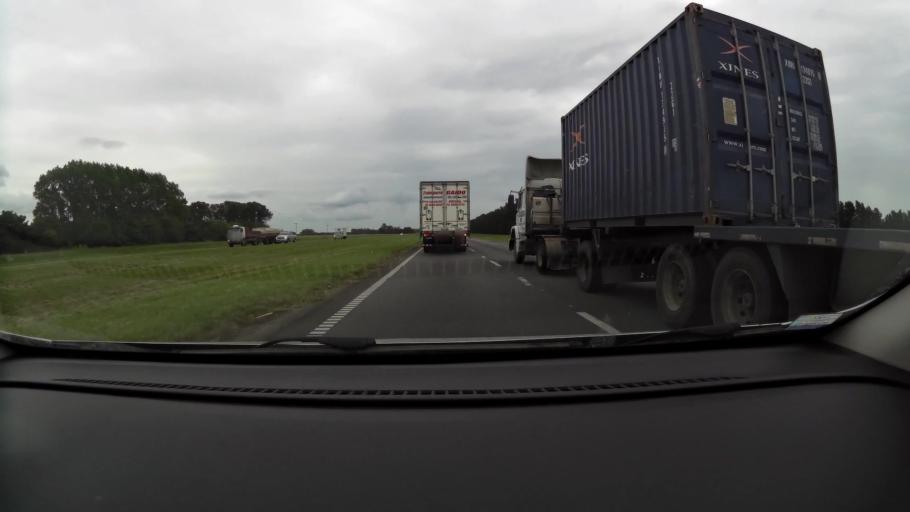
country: AR
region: Buenos Aires
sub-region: Partido de Baradero
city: Baradero
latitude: -33.8886
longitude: -59.4885
